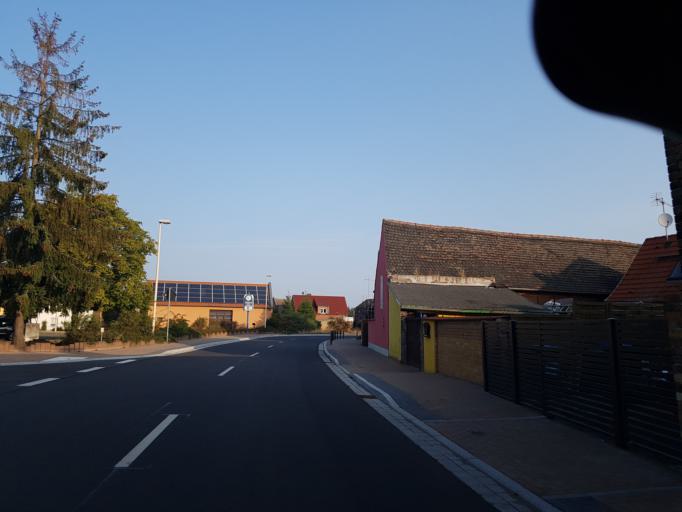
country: DE
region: Saxony-Anhalt
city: Bad Schmiedeberg
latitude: 51.7485
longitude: 12.7495
